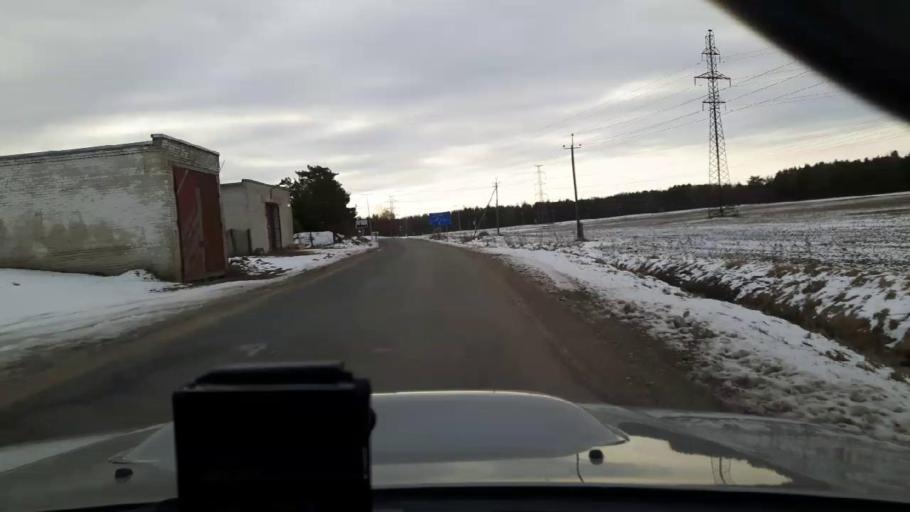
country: EE
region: Harju
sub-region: Saue vald
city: Laagri
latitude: 59.3487
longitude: 24.5993
